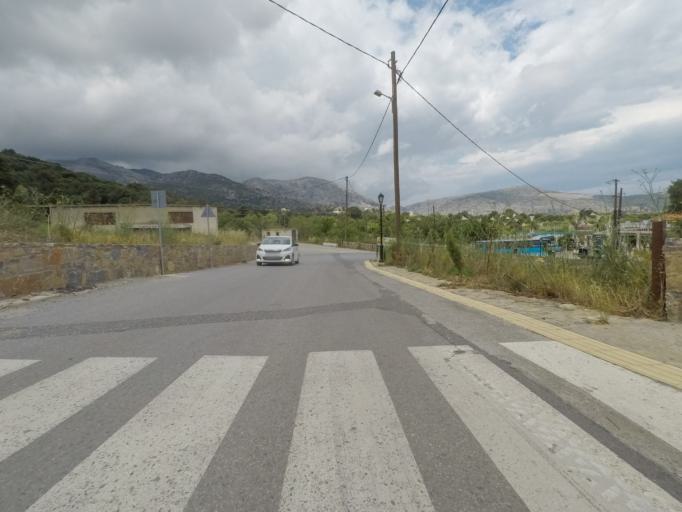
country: GR
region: Crete
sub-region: Nomos Irakleiou
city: Mokhos
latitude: 35.1665
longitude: 25.4497
